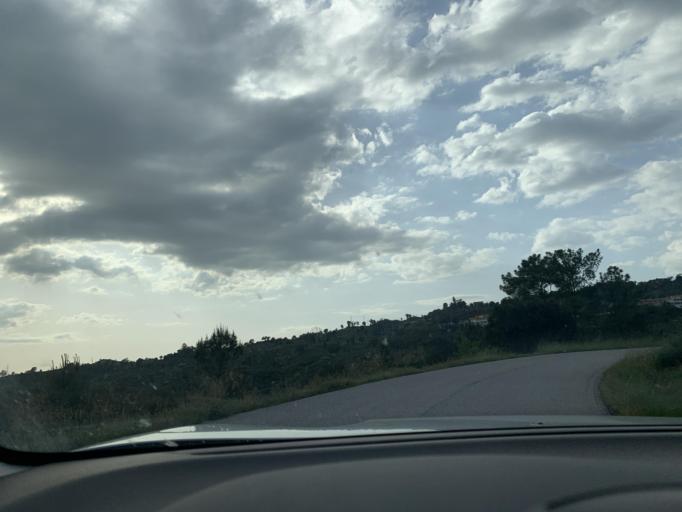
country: PT
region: Guarda
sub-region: Fornos de Algodres
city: Fornos de Algodres
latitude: 40.5689
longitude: -7.5983
